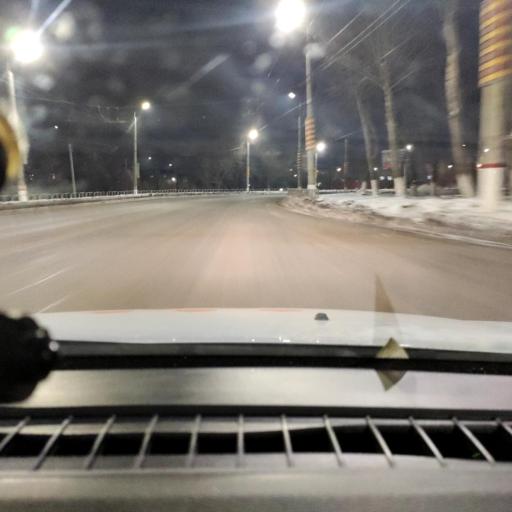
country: RU
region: Samara
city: Novokuybyshevsk
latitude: 53.0865
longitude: 49.9531
